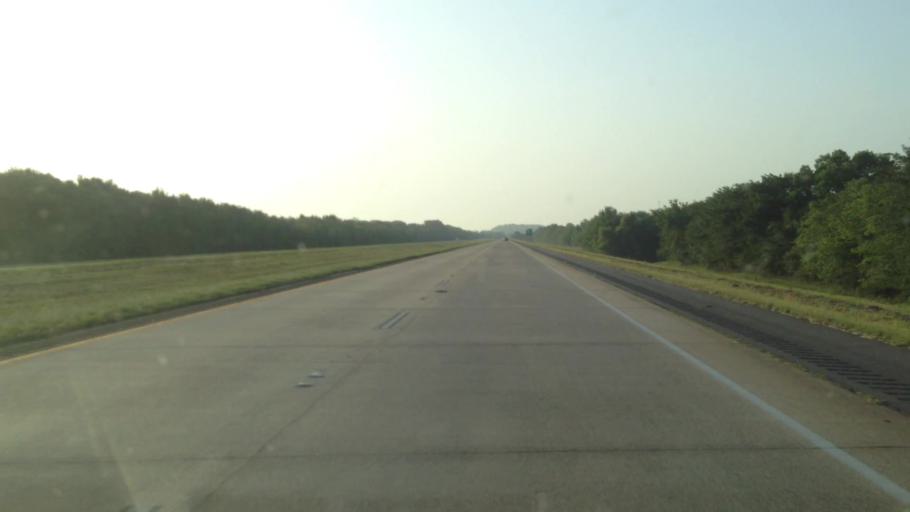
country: US
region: Louisiana
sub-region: Grant Parish
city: Colfax
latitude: 31.5072
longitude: -92.8873
